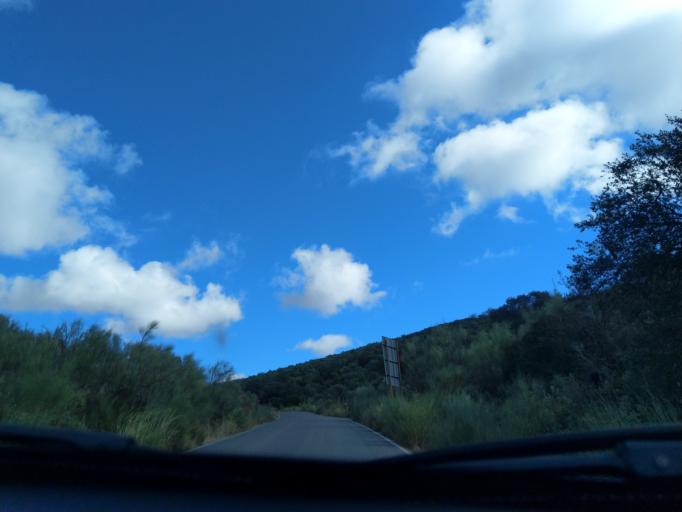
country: ES
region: Extremadura
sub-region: Provincia de Badajoz
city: Reina
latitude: 38.1445
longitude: -5.9152
